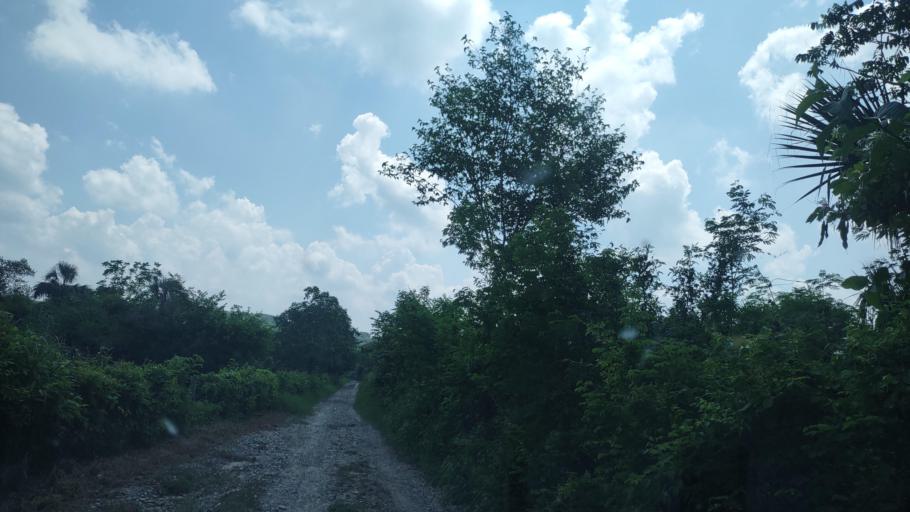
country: MX
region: Veracruz
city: Tempoal de Sanchez
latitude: 21.5461
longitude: -98.2730
